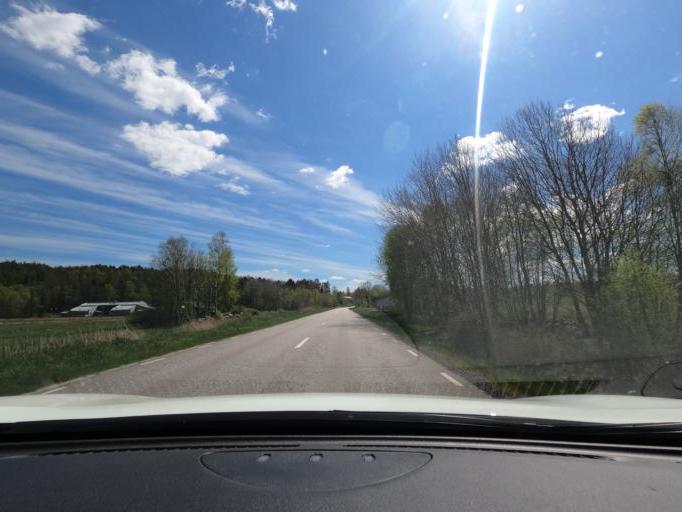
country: SE
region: Halland
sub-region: Kungsbacka Kommun
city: Fjaeras kyrkby
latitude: 57.3964
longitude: 12.2407
